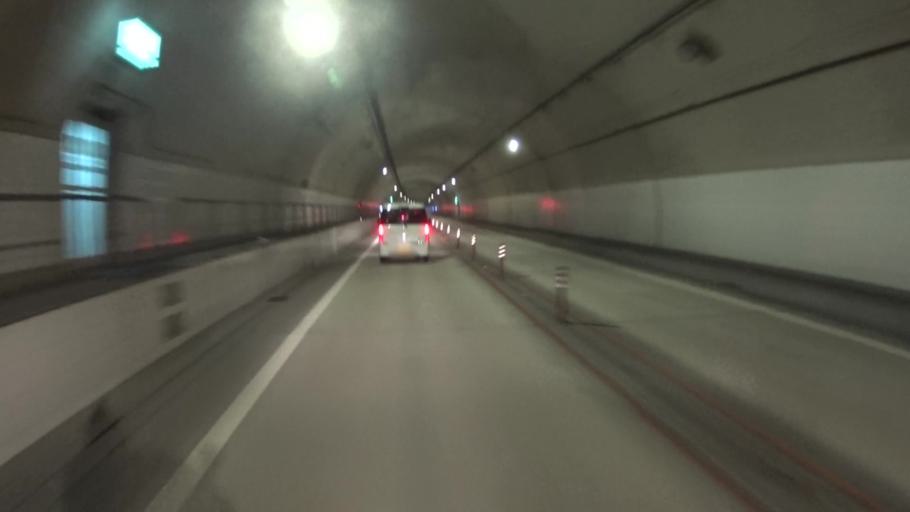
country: JP
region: Kyoto
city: Miyazu
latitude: 35.5230
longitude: 135.1812
